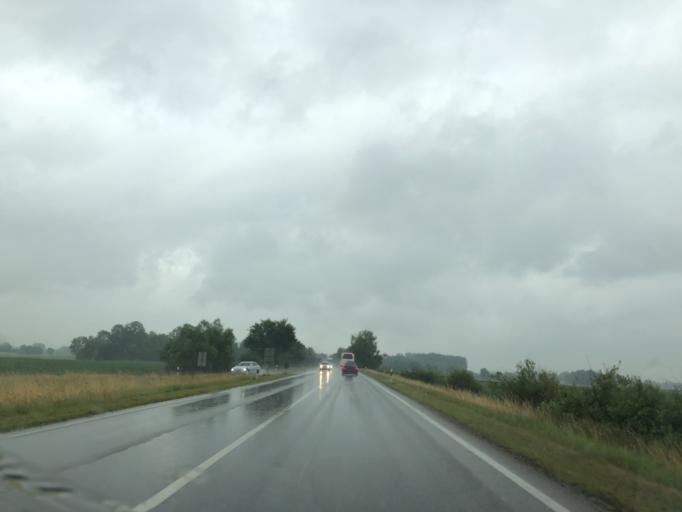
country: DE
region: Bavaria
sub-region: Upper Bavaria
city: Oberding
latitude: 48.3561
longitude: 11.8526
